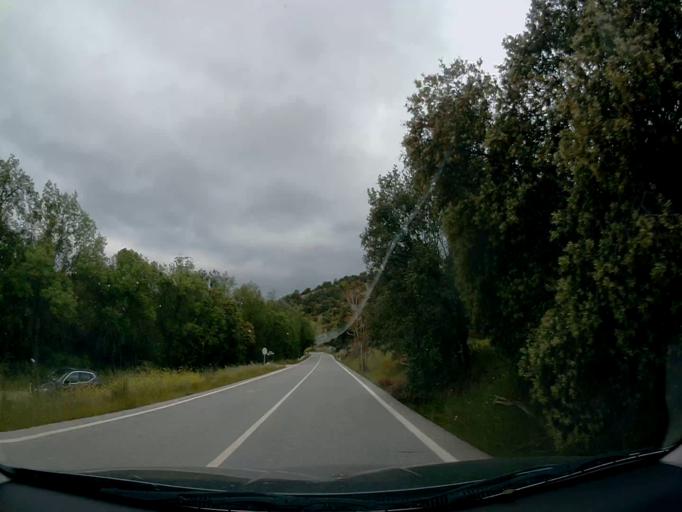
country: ES
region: Madrid
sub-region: Provincia de Madrid
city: Navalagamella
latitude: 40.4380
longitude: -4.1106
